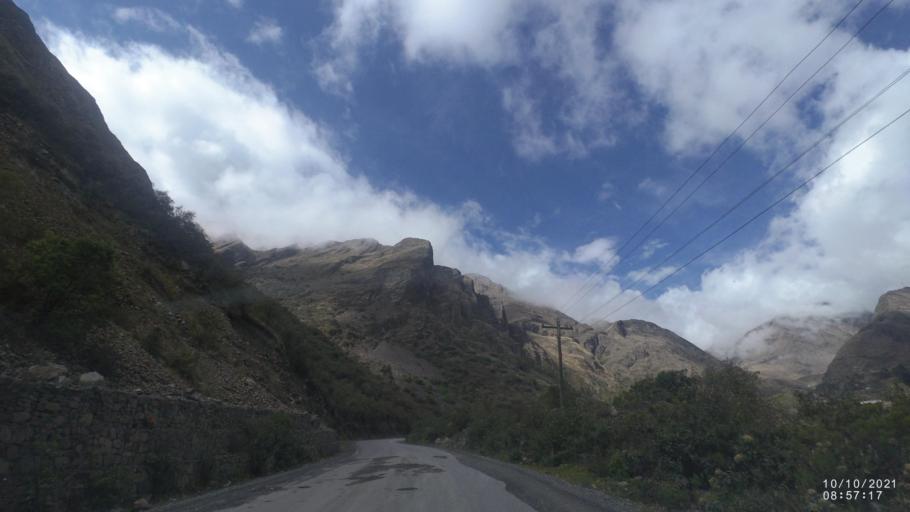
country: BO
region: La Paz
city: Quime
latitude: -16.9937
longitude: -67.2495
